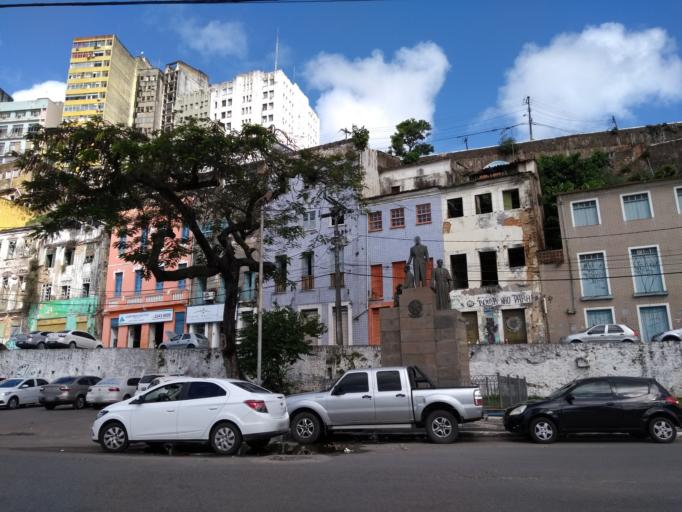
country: BR
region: Bahia
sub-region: Salvador
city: Salvador
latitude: -12.9760
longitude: -38.5155
